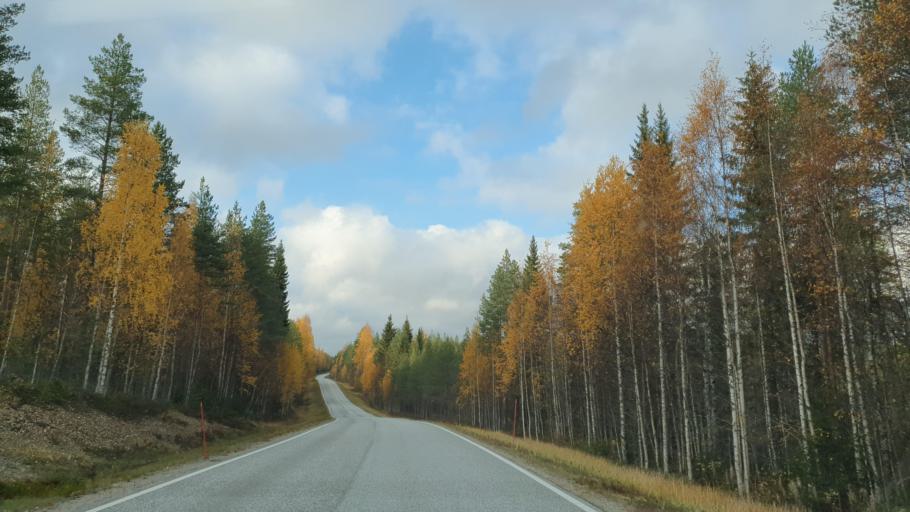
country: FI
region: Kainuu
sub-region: Kehys-Kainuu
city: Kuhmo
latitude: 64.3293
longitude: 29.4912
